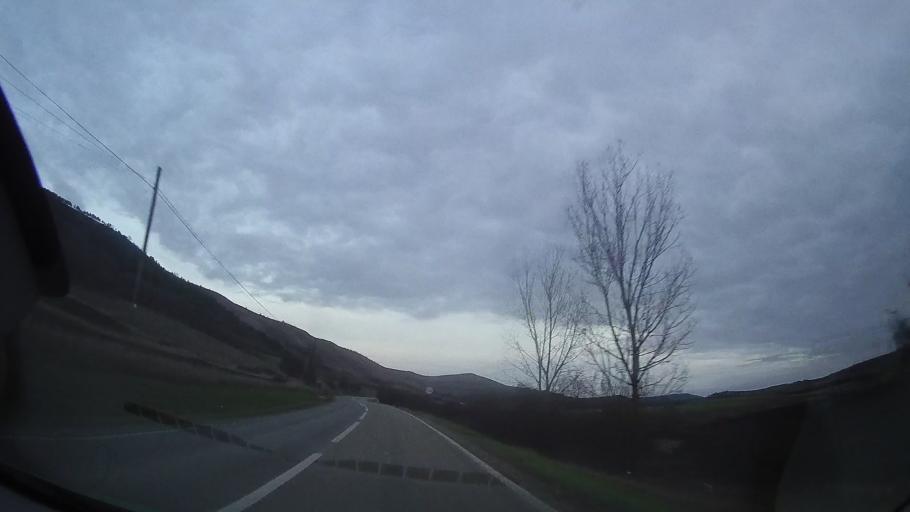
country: RO
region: Cluj
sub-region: Comuna Caianu
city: Caianu
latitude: 46.8015
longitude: 23.9346
